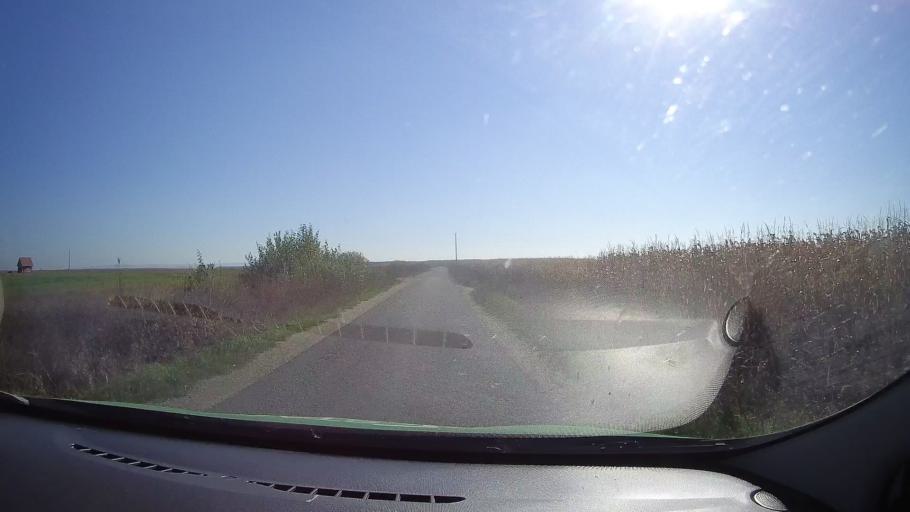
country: RO
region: Satu Mare
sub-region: Comuna Doba
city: Doba
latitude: 47.7379
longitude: 22.7192
